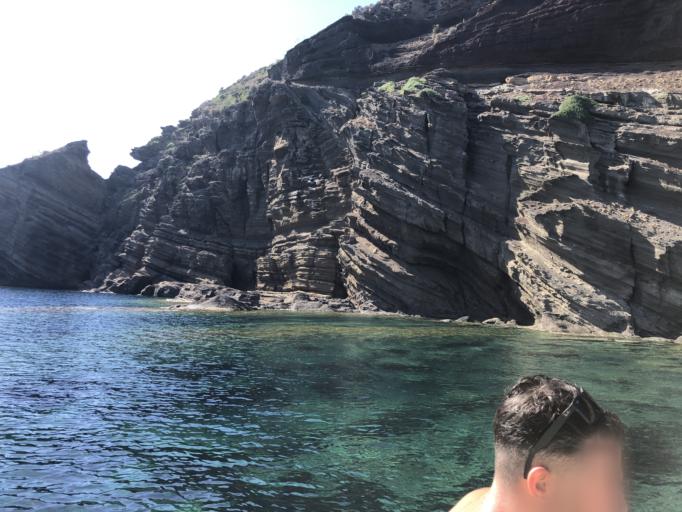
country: IT
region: Sicily
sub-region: Agrigento
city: Lampedusa
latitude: 35.8552
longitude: 12.8792
